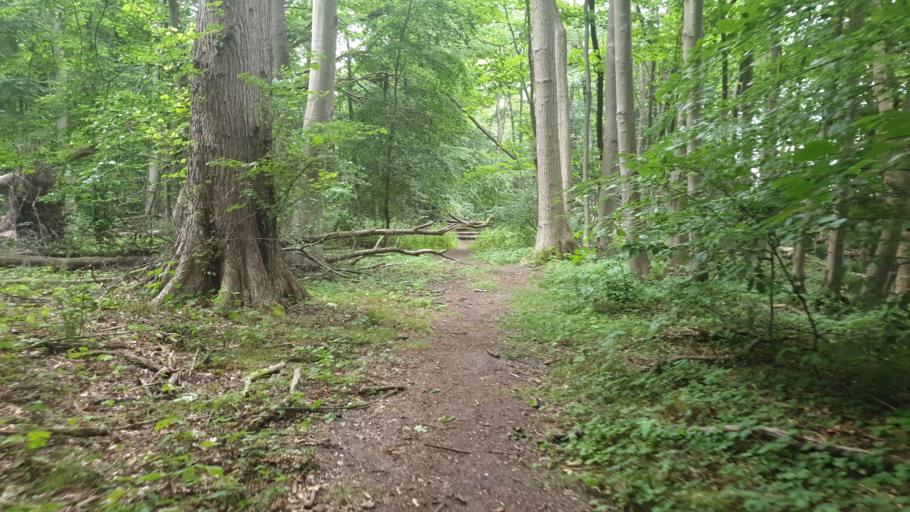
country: DE
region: Mecklenburg-Vorpommern
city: Werdervorstadt
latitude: 53.6443
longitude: 11.4528
